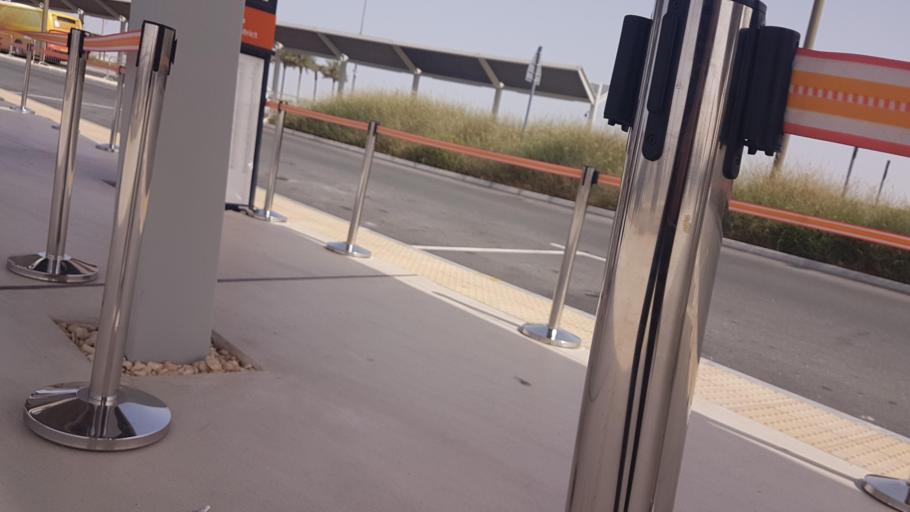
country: AE
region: Dubai
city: Dubai
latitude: 24.9671
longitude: 55.1557
